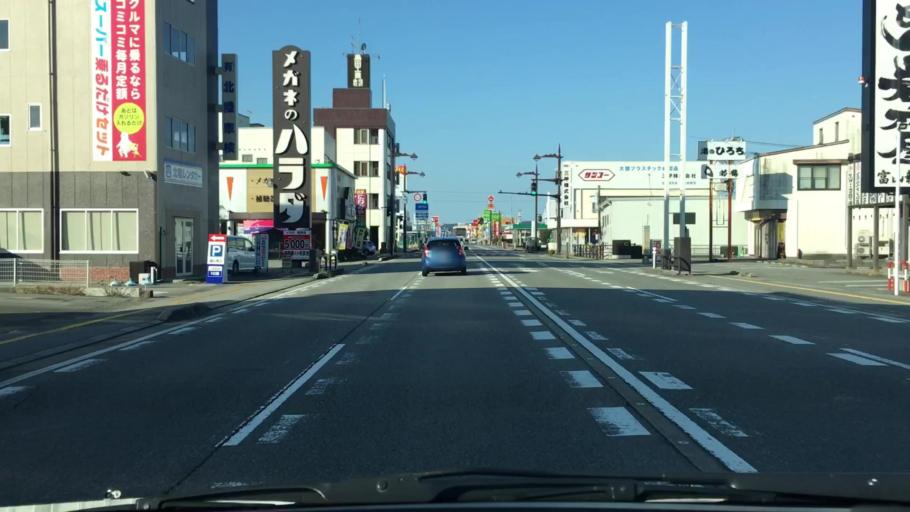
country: JP
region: Toyama
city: Toyama-shi
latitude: 36.6963
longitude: 137.2500
